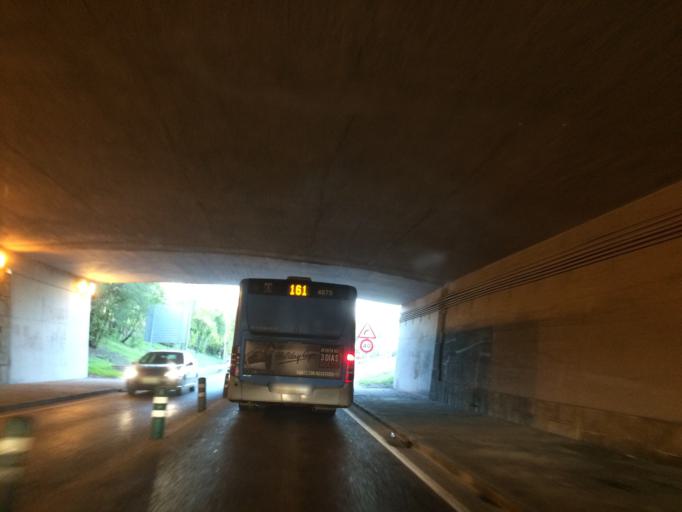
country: ES
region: Madrid
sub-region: Provincia de Madrid
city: Moncloa-Aravaca
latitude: 40.4621
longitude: -3.7711
